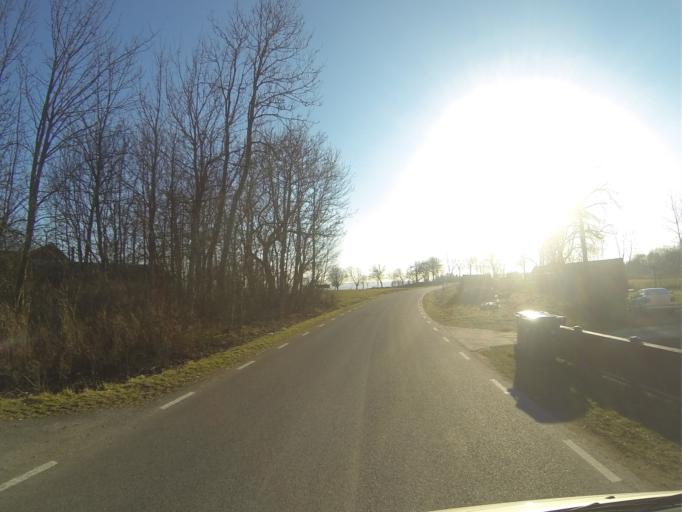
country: SE
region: Skane
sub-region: Hoors Kommun
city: Loberod
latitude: 55.7501
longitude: 13.4621
